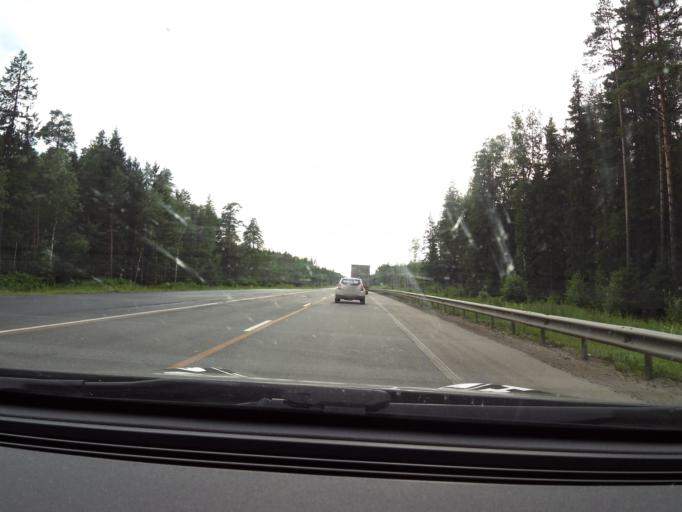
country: RU
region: Vladimir
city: Mstera
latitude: 56.2343
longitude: 41.8372
